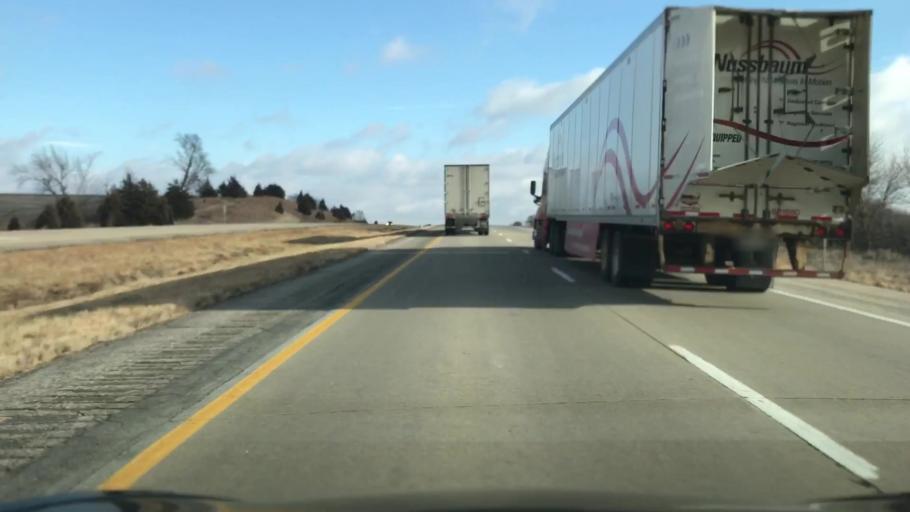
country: US
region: Iowa
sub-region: Cass County
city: Atlantic
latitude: 41.4970
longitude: -94.9193
